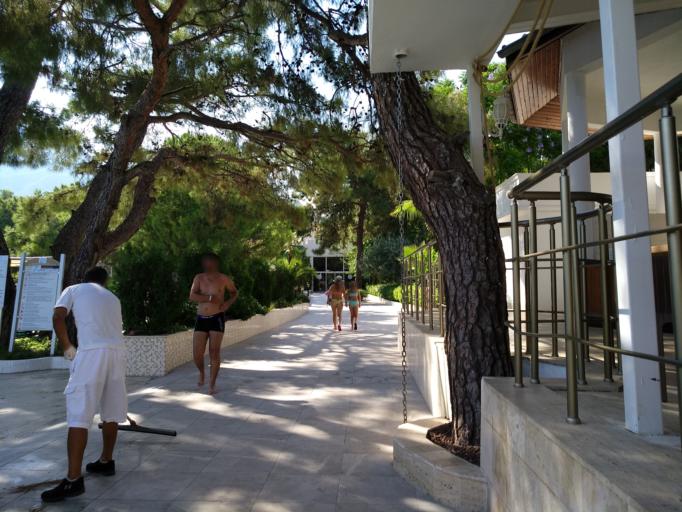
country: TR
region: Antalya
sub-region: Kemer
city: Goeynuek
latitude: 36.6656
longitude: 30.5629
